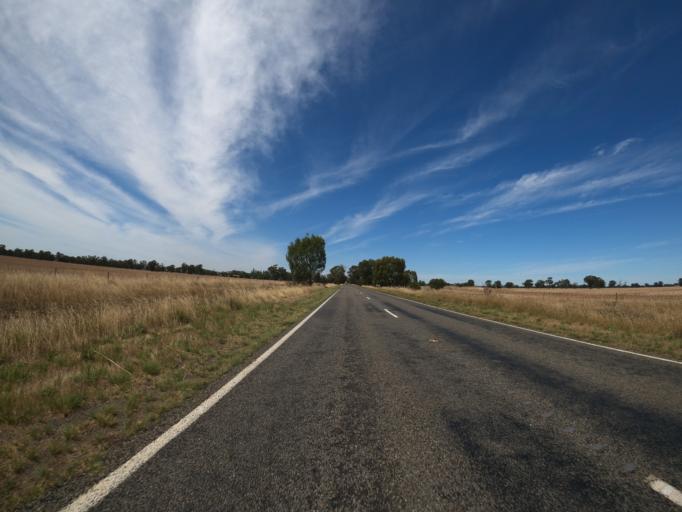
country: AU
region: Victoria
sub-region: Benalla
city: Benalla
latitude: -36.2860
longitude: 145.9523
